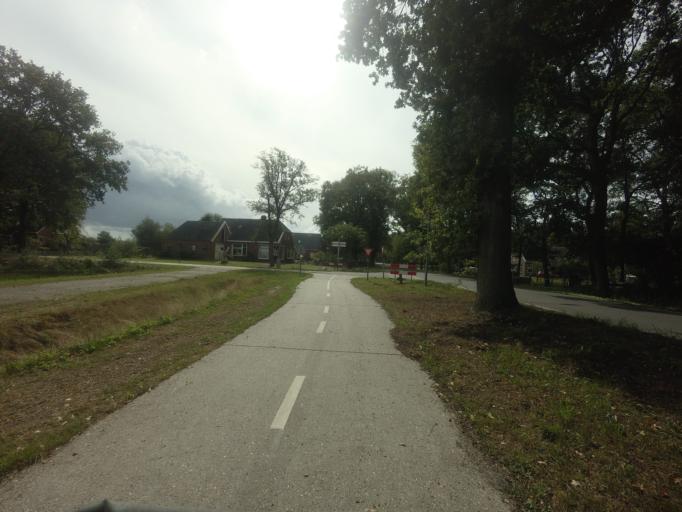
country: NL
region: Drenthe
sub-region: Gemeente Assen
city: Assen
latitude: 53.0480
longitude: 6.4567
